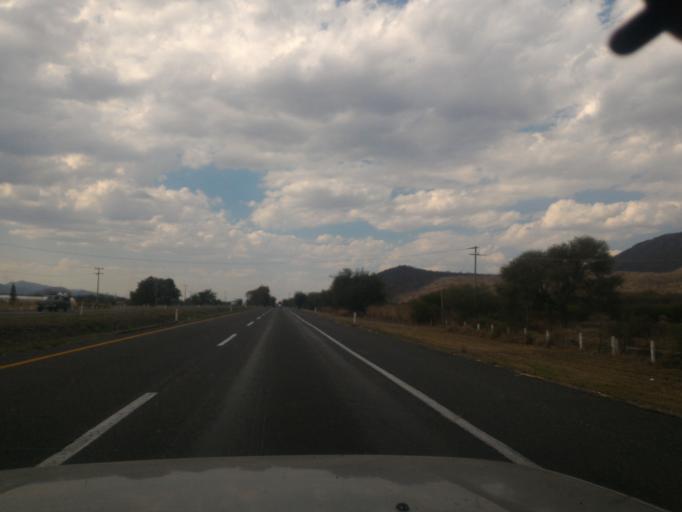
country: MX
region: Jalisco
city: Zacoalco de Torres
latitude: 20.1834
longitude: -103.5135
